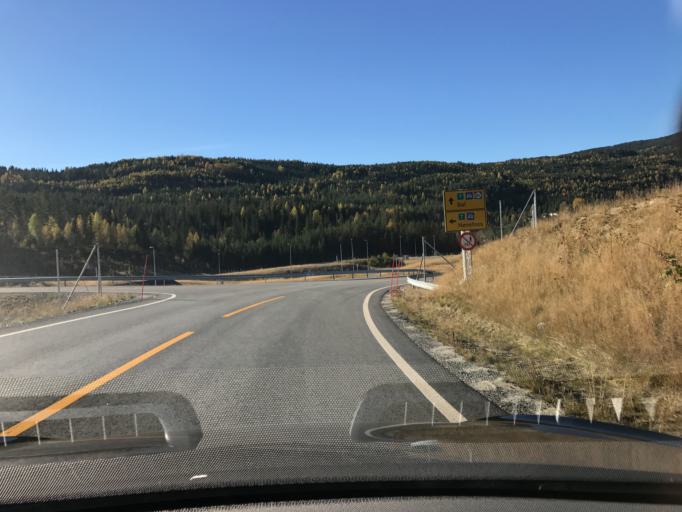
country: NO
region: Buskerud
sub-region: Krodsherad
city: Noresund
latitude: 60.2672
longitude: 9.7966
